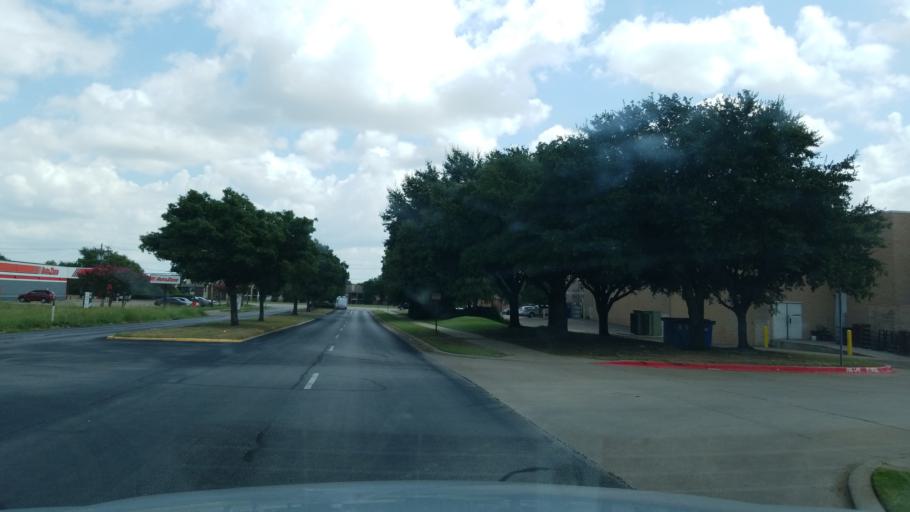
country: US
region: Texas
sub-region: Tarrant County
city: Euless
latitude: 32.8540
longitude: -97.0843
